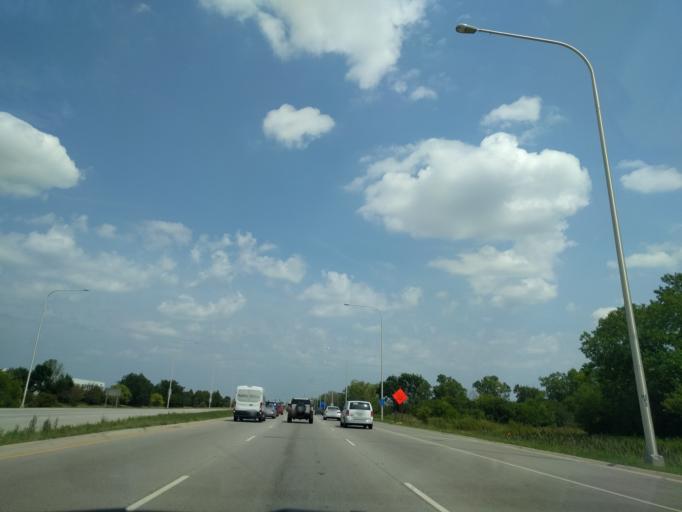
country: US
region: Illinois
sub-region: Cook County
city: Schiller Park
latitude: 41.9583
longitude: -87.8832
